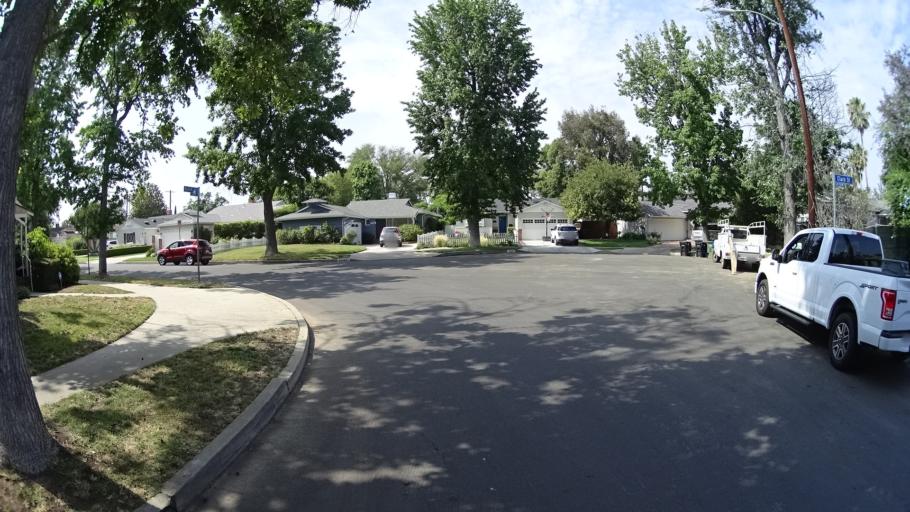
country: US
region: California
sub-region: Los Angeles County
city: Sherman Oaks
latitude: 34.1684
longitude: -118.4543
